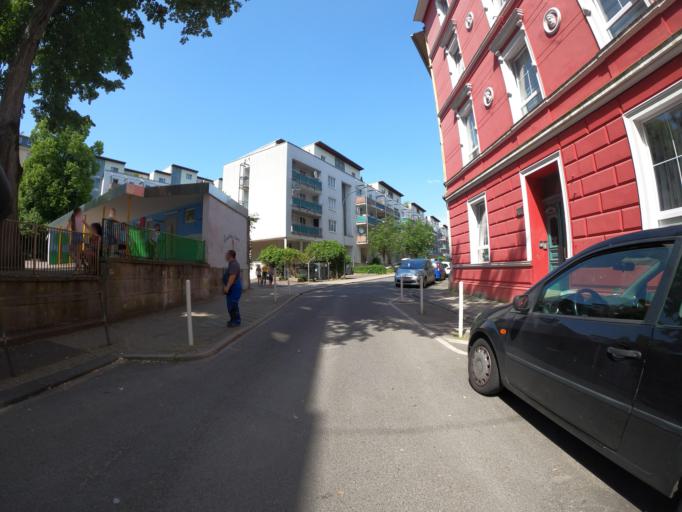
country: DE
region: North Rhine-Westphalia
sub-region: Regierungsbezirk Dusseldorf
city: Wuppertal
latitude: 51.2649
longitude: 7.1554
